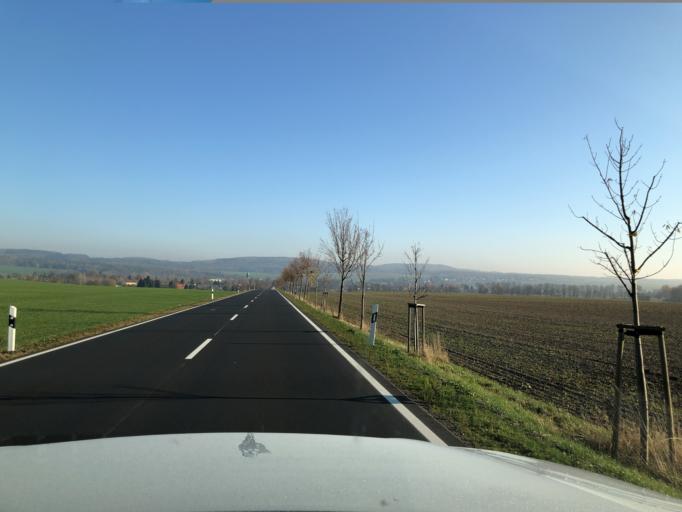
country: DE
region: Saxony
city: Lohmen
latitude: 50.9826
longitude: 13.9795
